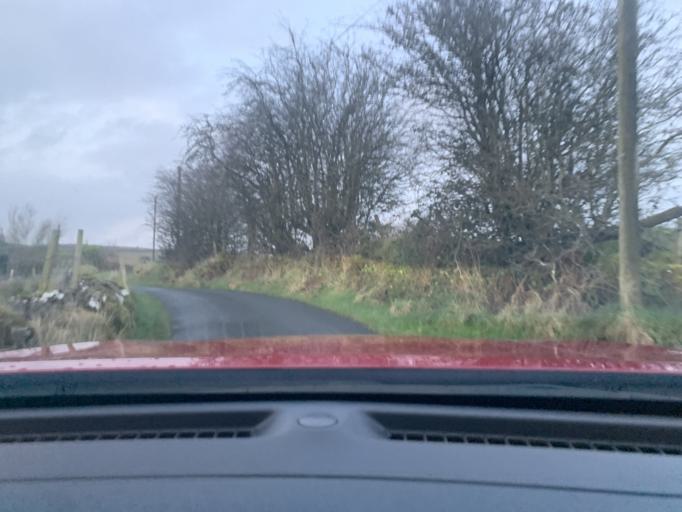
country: IE
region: Connaught
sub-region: Sligo
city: Ballymote
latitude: 54.0463
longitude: -8.4069
